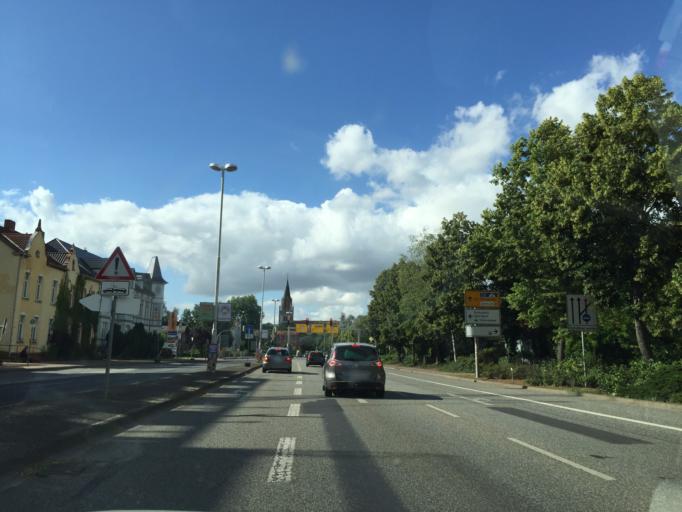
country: DE
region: Mecklenburg-Vorpommern
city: Neubrandenburg
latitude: 53.5504
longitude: 13.2637
